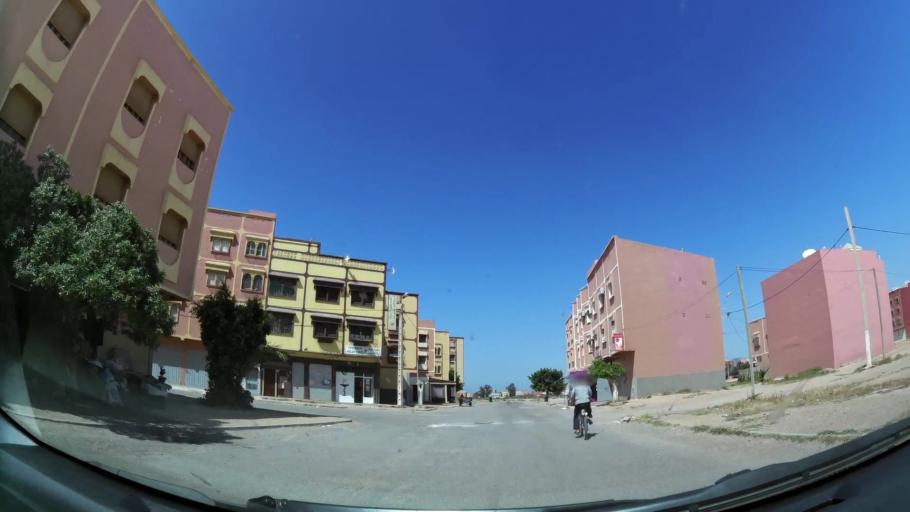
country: MA
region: Souss-Massa-Draa
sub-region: Inezgane-Ait Mellou
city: Inezgane
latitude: 30.3349
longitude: -9.5083
